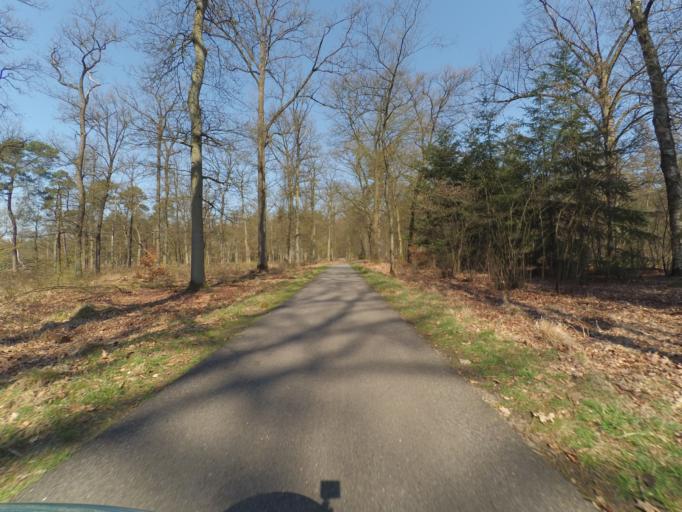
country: NL
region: Gelderland
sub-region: Gemeente Ede
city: Otterlo
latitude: 52.1080
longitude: 5.8487
